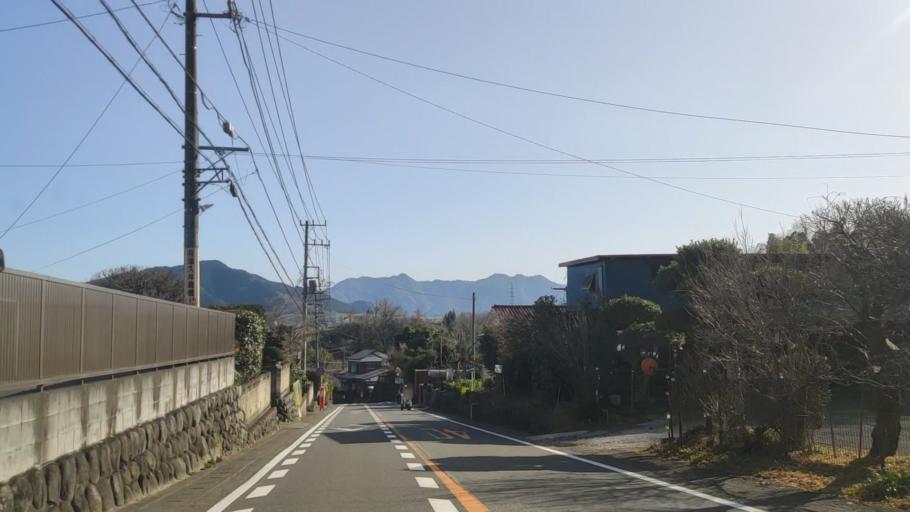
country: JP
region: Tokyo
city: Hachioji
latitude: 35.5798
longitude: 139.2726
